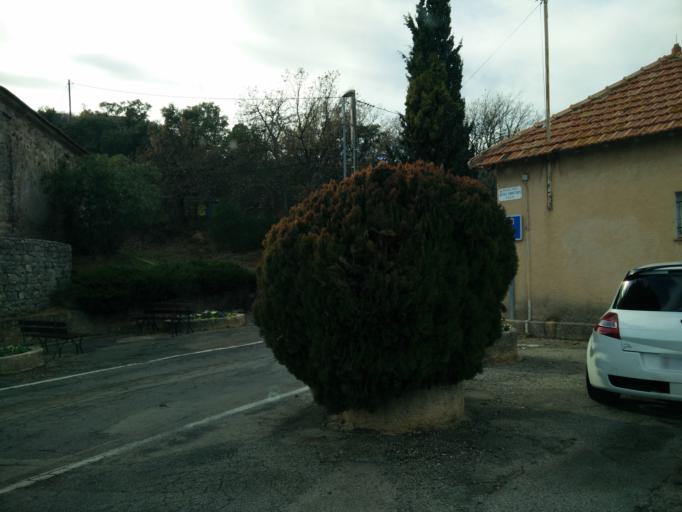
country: FR
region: Provence-Alpes-Cote d'Azur
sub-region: Departement du Var
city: Roquebrune-sur-Argens
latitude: 43.4400
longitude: 6.6339
